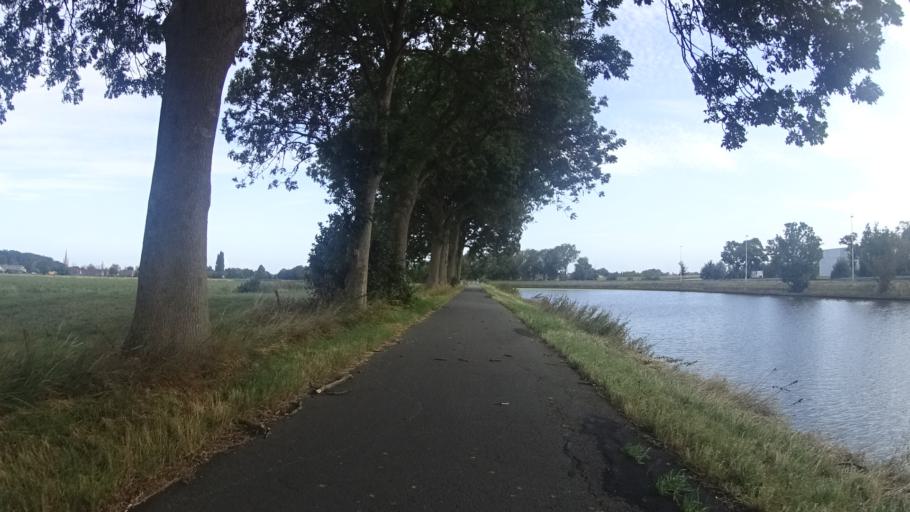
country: BE
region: Flanders
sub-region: Provincie West-Vlaanderen
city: Ieper
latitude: 50.8906
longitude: 2.8690
